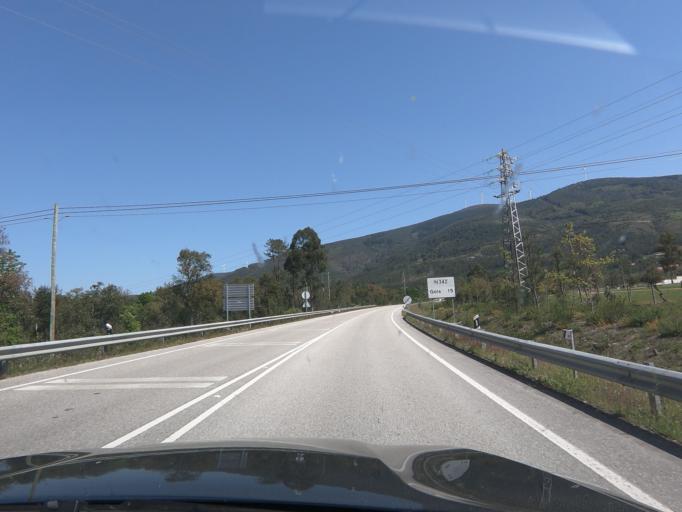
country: PT
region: Coimbra
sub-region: Lousa
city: Lousa
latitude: 40.1257
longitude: -8.2351
